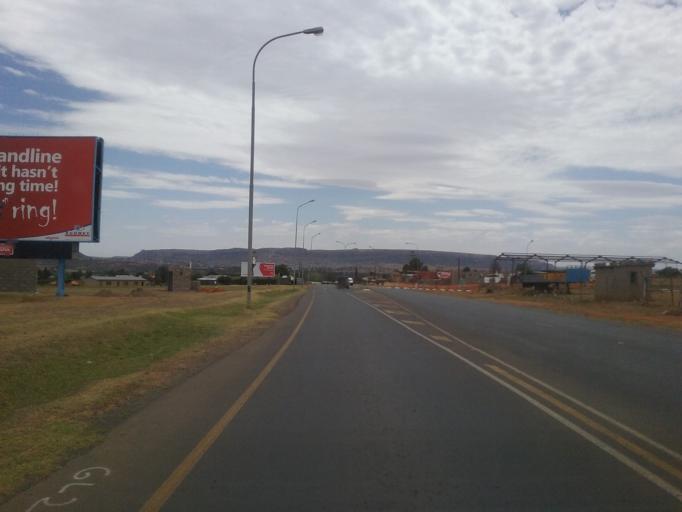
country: LS
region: Maseru
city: Maseru
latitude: -29.4244
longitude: 27.5618
